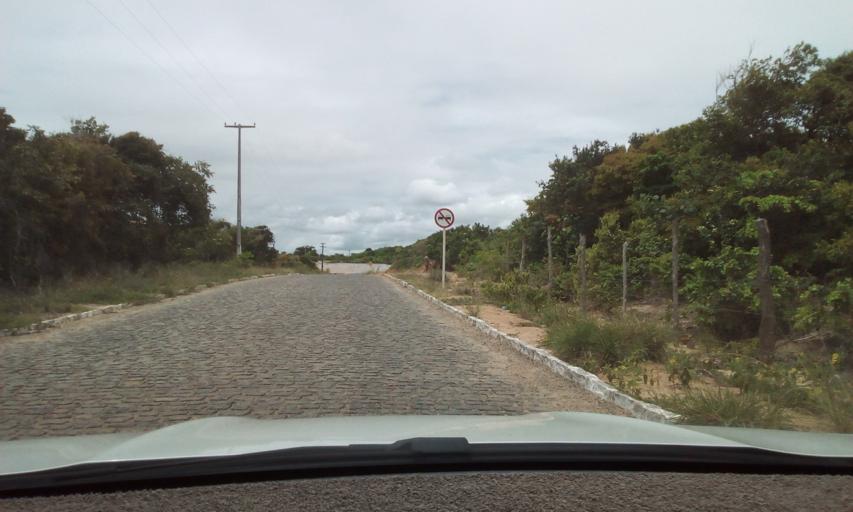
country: BR
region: Paraiba
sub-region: Conde
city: Conde
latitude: -7.3329
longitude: -34.8018
